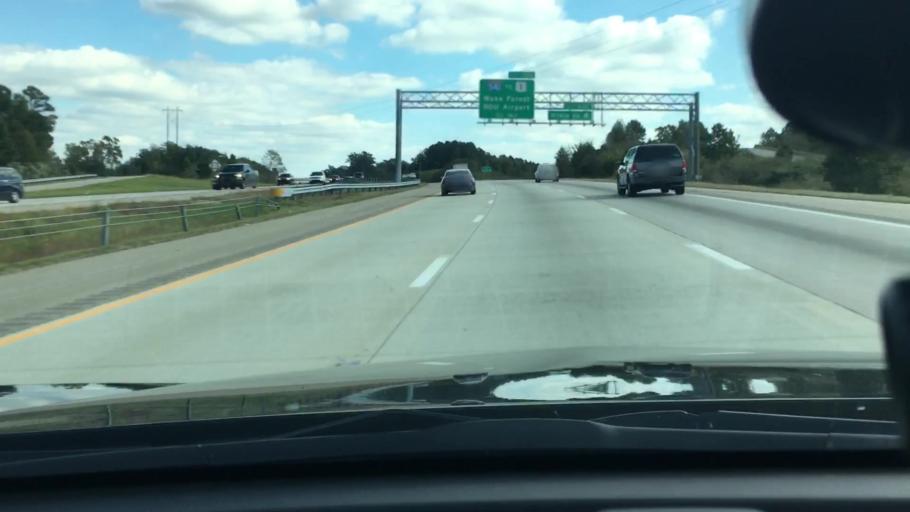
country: US
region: North Carolina
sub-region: Wake County
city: Knightdale
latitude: 35.7694
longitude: -78.5280
